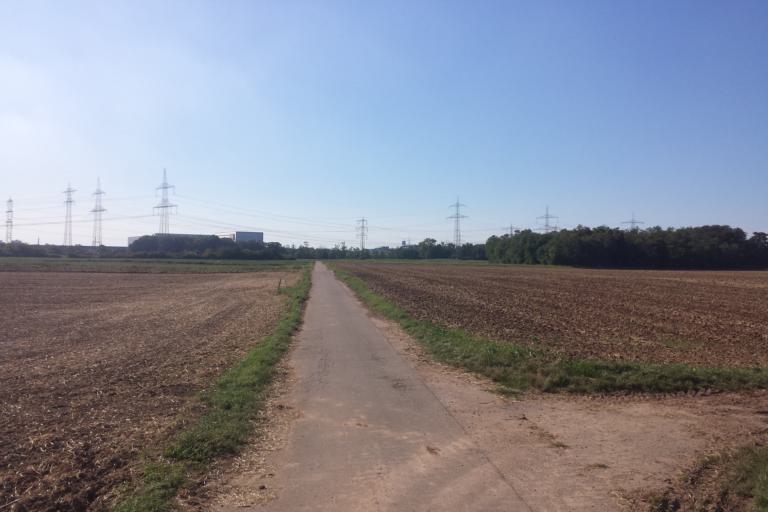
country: DE
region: Hesse
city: Viernheim
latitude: 49.5137
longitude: 8.5711
